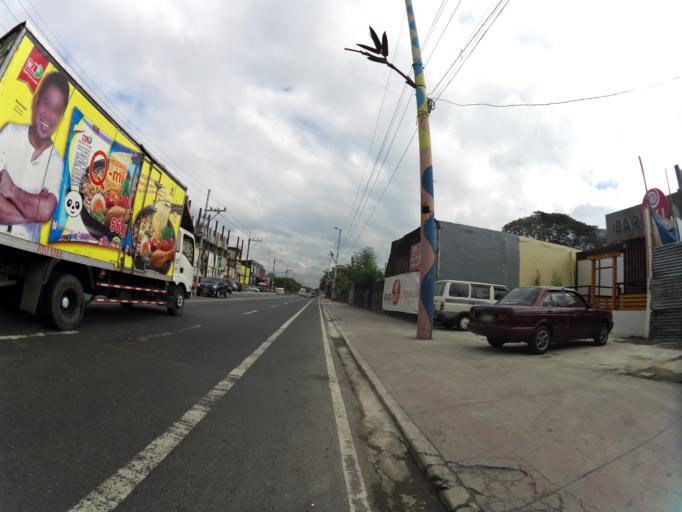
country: PH
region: Metro Manila
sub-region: Marikina
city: Calumpang
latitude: 14.6373
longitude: 121.1020
